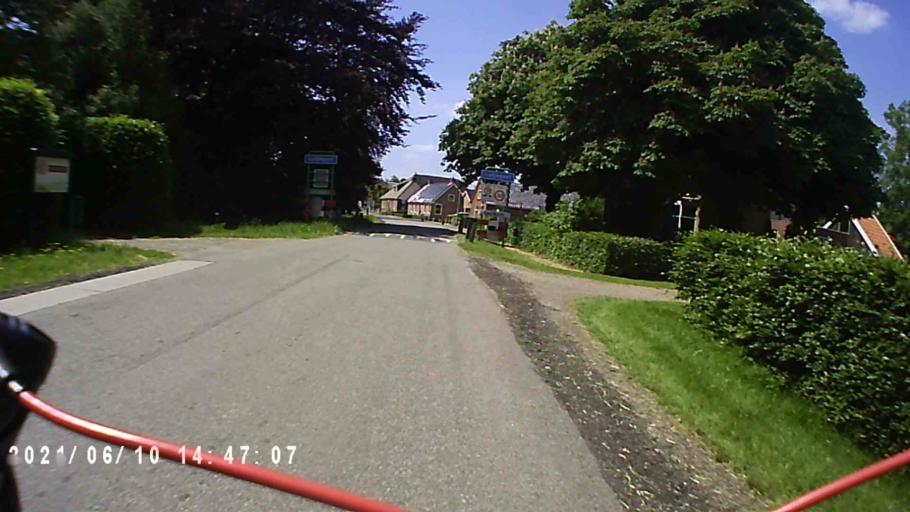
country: NL
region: Groningen
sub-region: Gemeente Grootegast
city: Grootegast
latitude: 53.2361
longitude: 6.2681
